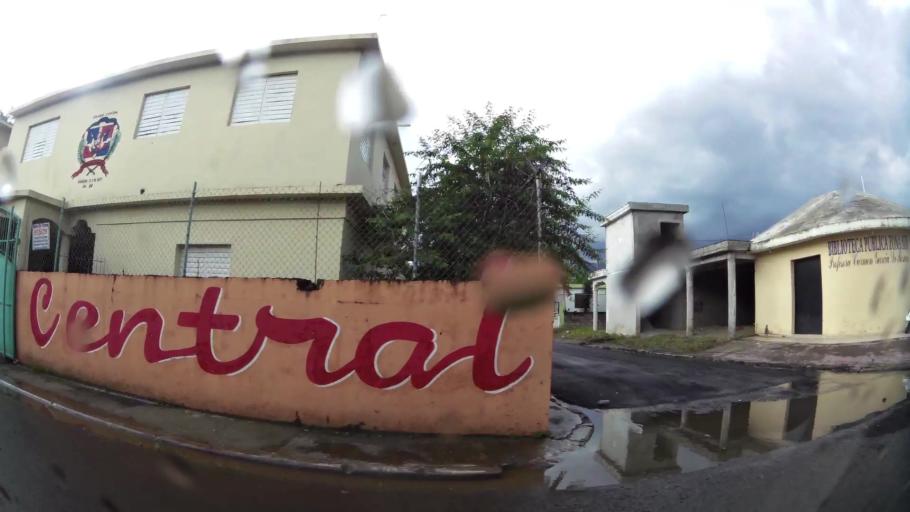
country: DO
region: Monsenor Nouel
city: Bonao
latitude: 18.9346
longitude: -70.3987
